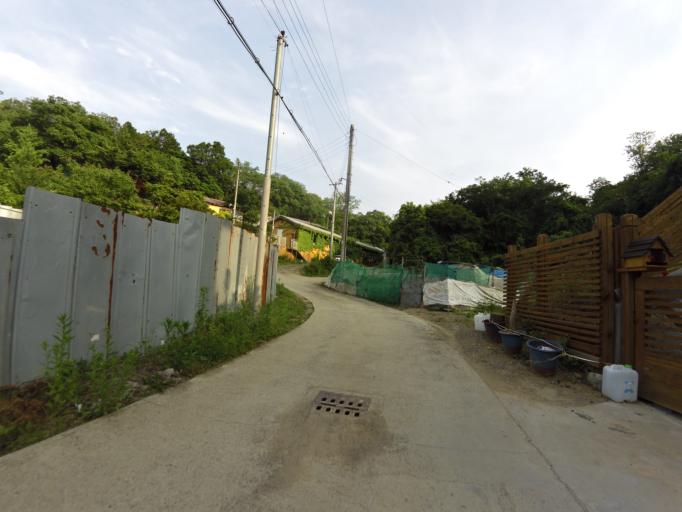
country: KR
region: Daegu
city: Daegu
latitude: 35.8600
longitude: 128.6502
